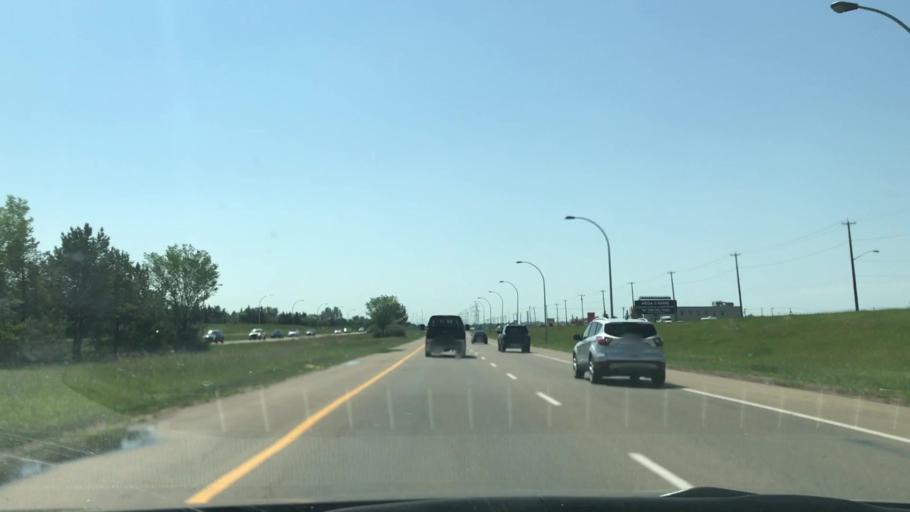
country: CA
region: Alberta
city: Edmonton
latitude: 53.4723
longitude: -113.4668
